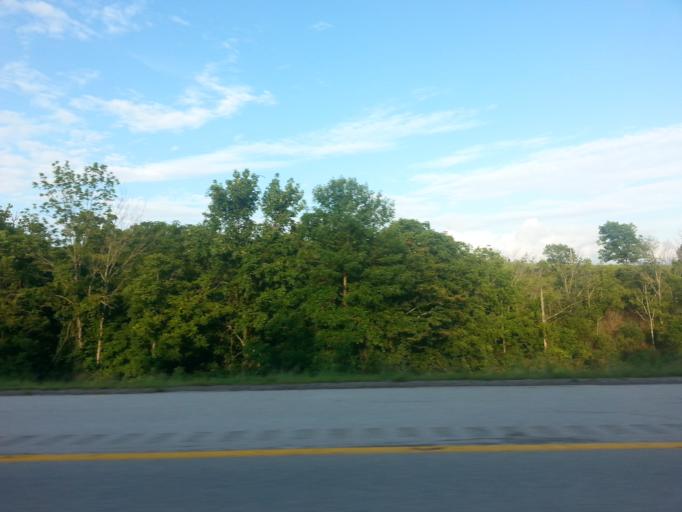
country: US
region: Kentucky
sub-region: Madison County
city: Berea
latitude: 37.6499
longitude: -84.3138
